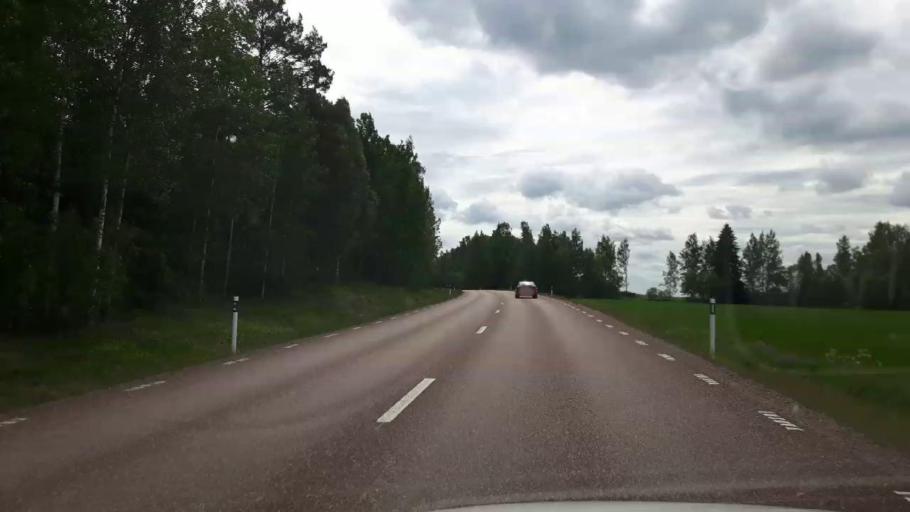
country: SE
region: Dalarna
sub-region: Hedemora Kommun
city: Hedemora
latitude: 60.3376
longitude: 15.9447
